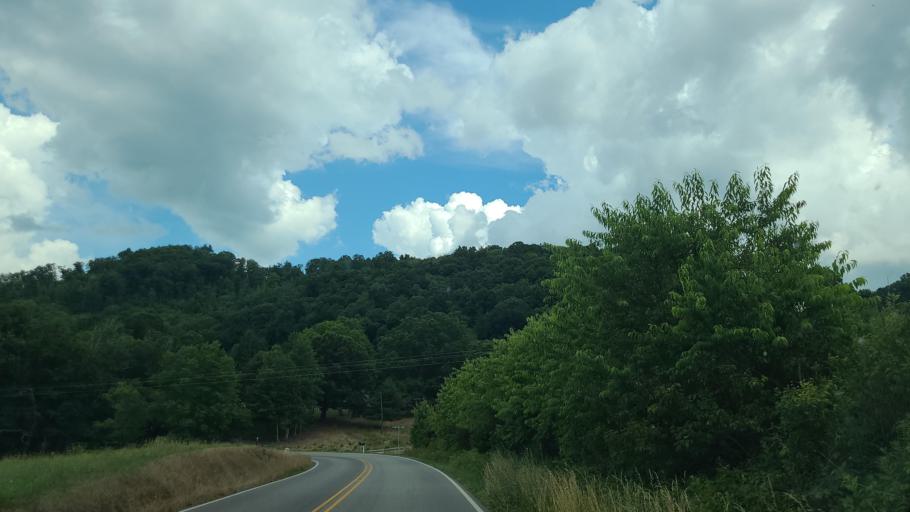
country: US
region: North Carolina
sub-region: Ashe County
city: Jefferson
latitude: 36.3986
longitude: -81.4020
